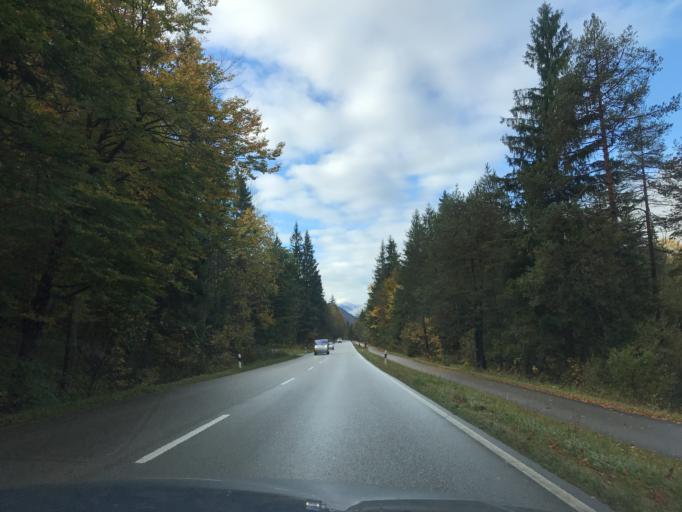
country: DE
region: Bavaria
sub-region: Upper Bavaria
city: Lenggries
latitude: 47.6197
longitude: 11.5933
